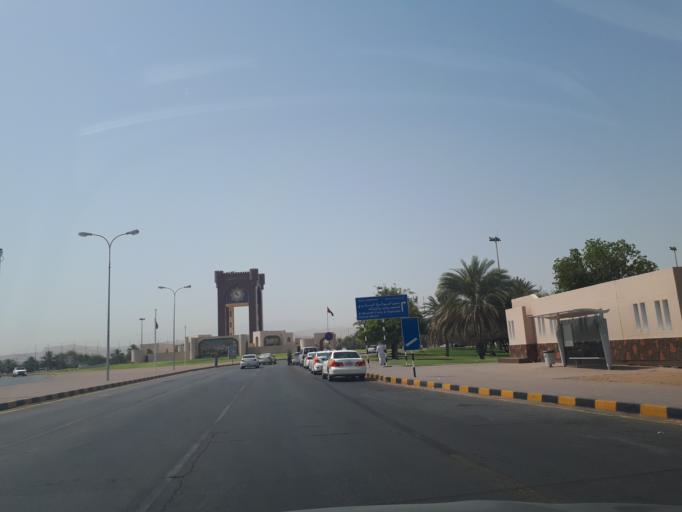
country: OM
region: Muhafazat Masqat
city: As Sib al Jadidah
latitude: 23.5889
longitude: 58.2515
